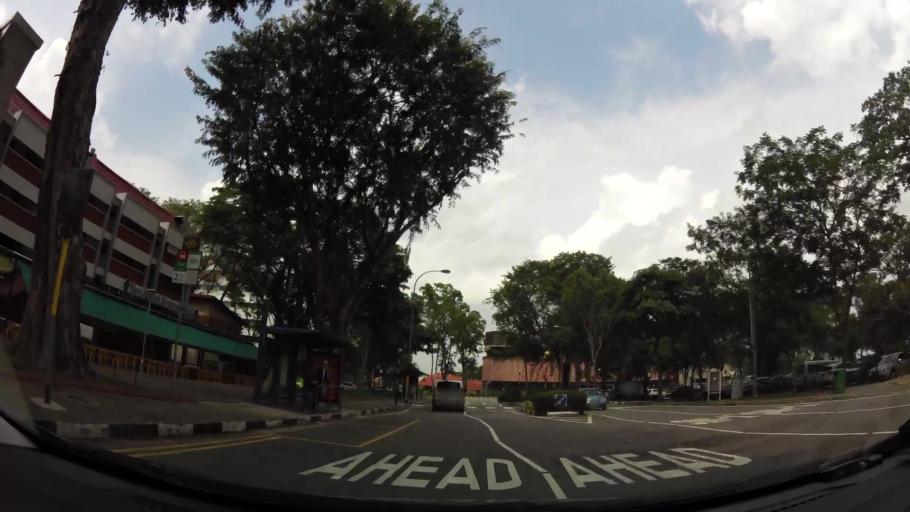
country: MY
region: Johor
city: Kampung Pasir Gudang Baru
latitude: 1.3896
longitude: 103.9869
